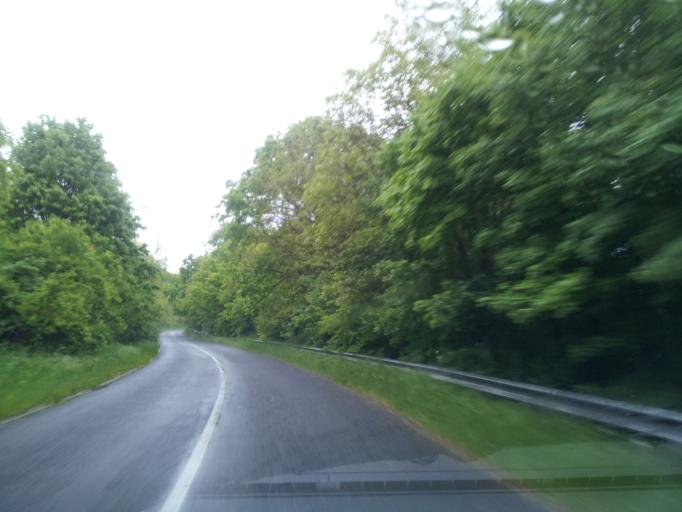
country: HU
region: Tolna
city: Bonyhad
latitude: 46.2568
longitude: 18.6079
